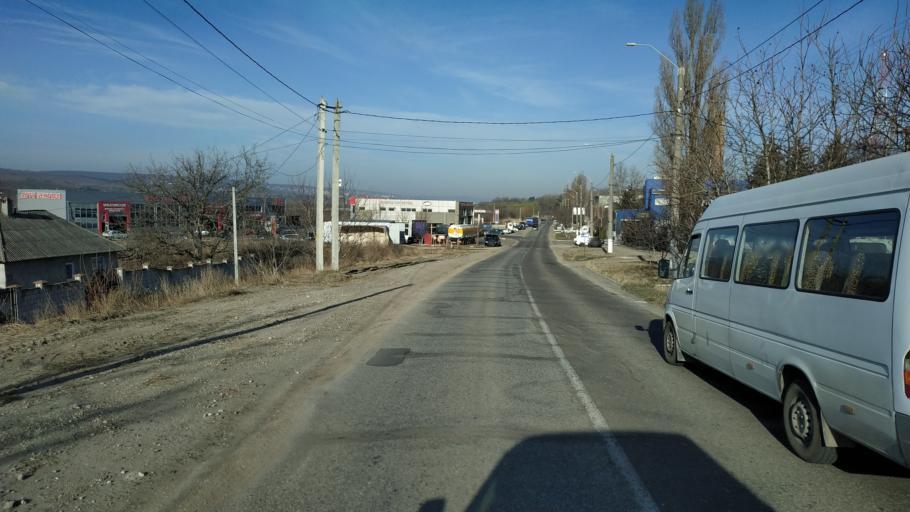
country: MD
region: Laloveni
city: Ialoveni
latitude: 46.9496
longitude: 28.7689
